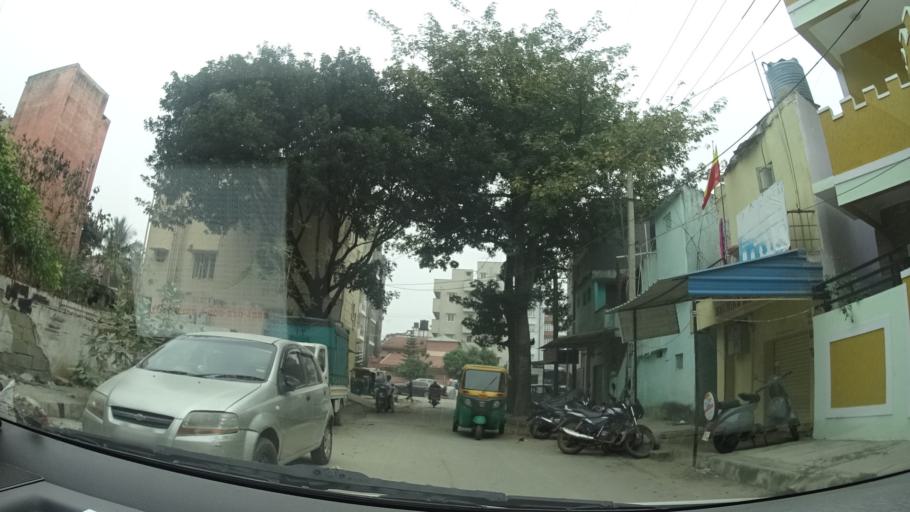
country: IN
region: Karnataka
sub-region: Bangalore Urban
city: Bangalore
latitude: 13.0336
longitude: 77.6313
